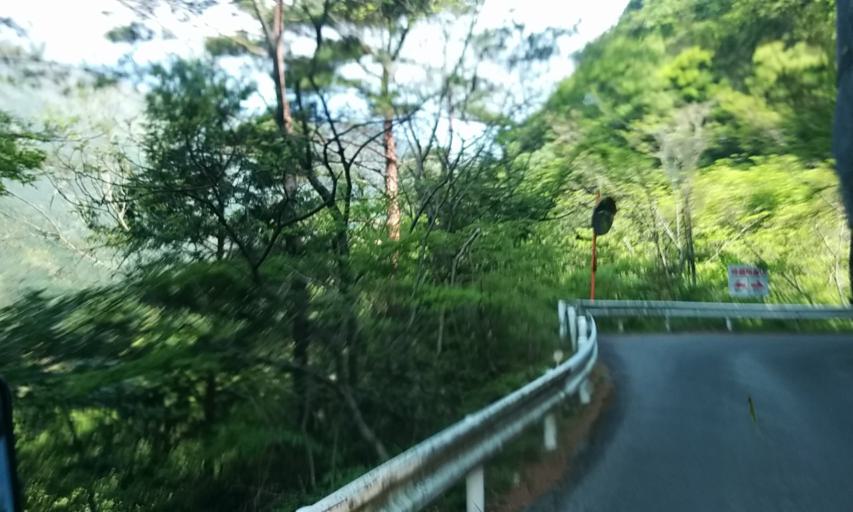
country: JP
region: Ehime
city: Niihama
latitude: 33.8734
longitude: 133.2964
